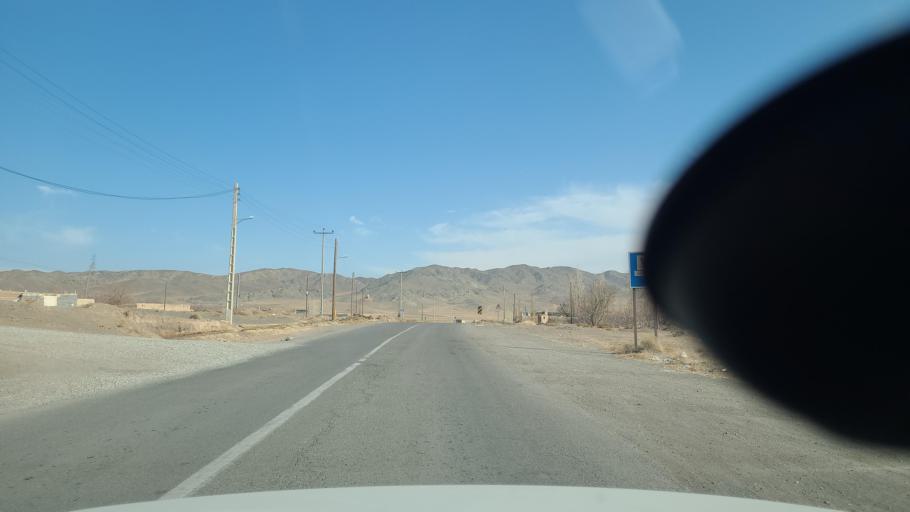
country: IR
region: Razavi Khorasan
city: Fariman
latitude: 35.5972
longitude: 59.6972
